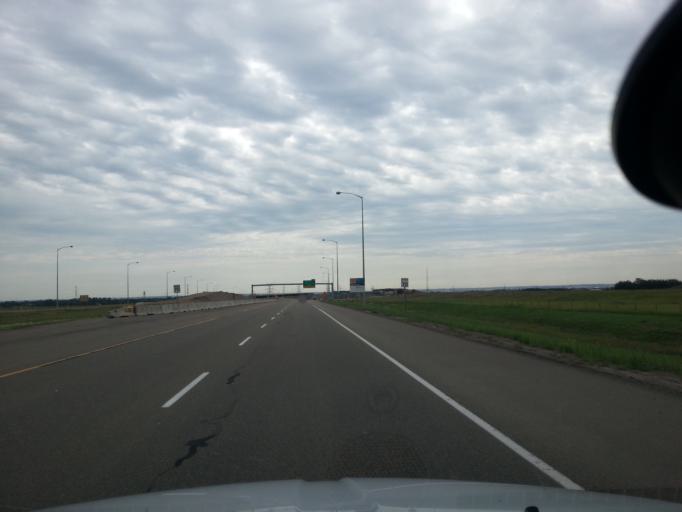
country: CA
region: Alberta
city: Edmonton
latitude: 53.6395
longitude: -113.4120
